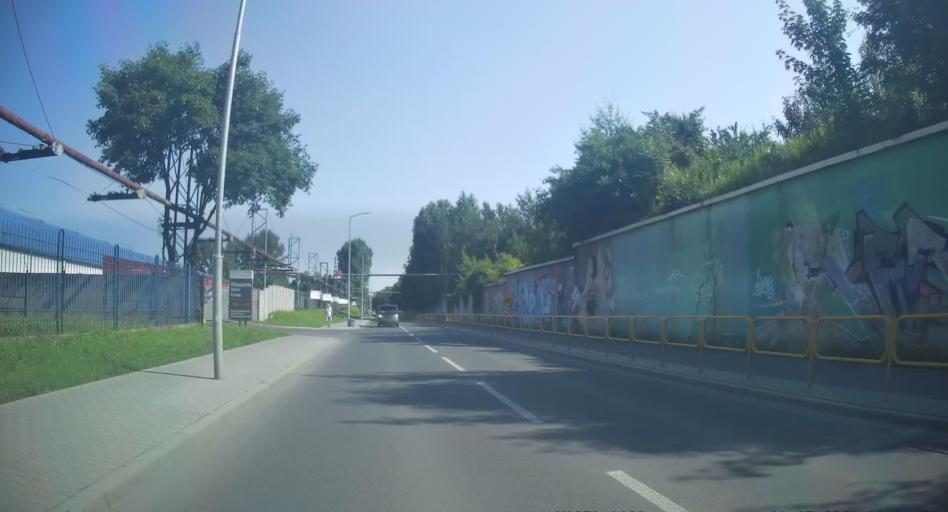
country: PL
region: Silesian Voivodeship
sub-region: Swietochlowice
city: Swietochlowice
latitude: 50.2855
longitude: 18.9135
